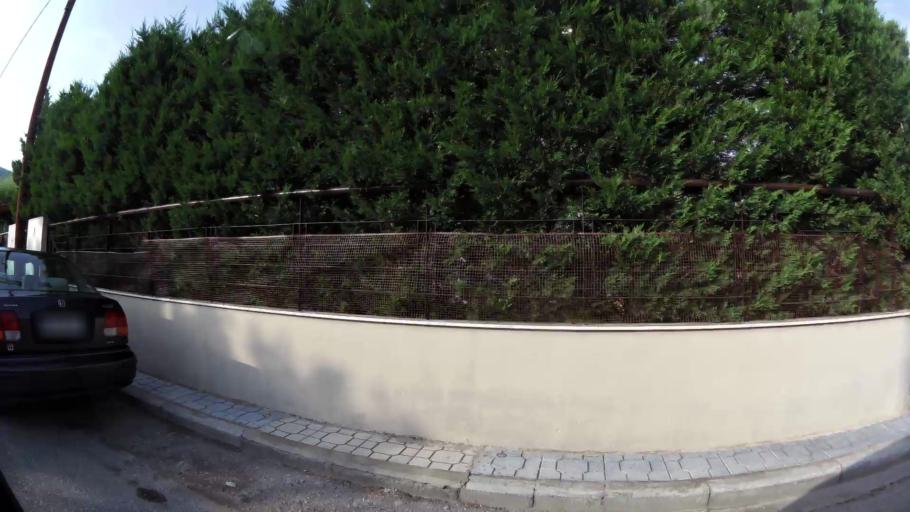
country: GR
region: Central Macedonia
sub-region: Nomos Thessalonikis
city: Oraiokastro
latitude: 40.7219
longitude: 22.9019
